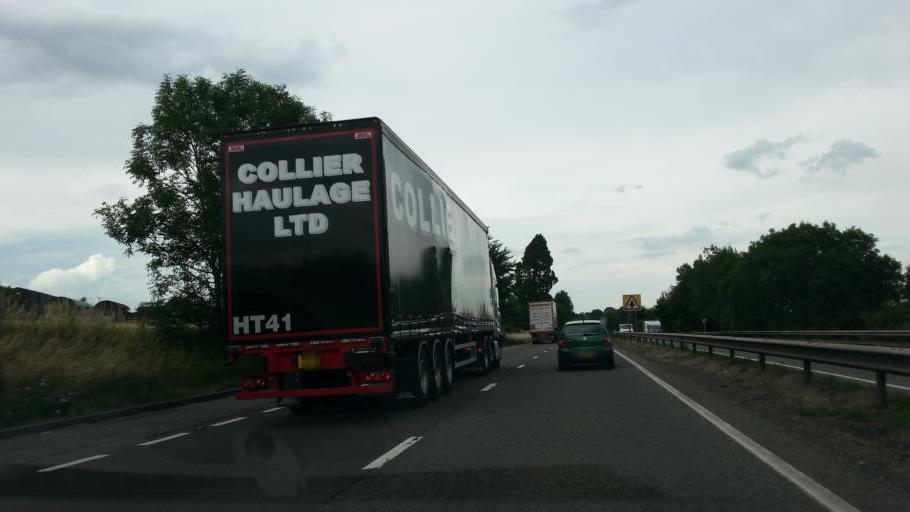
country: GB
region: England
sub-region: Herefordshire
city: Walford
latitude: 51.9078
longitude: -2.6207
